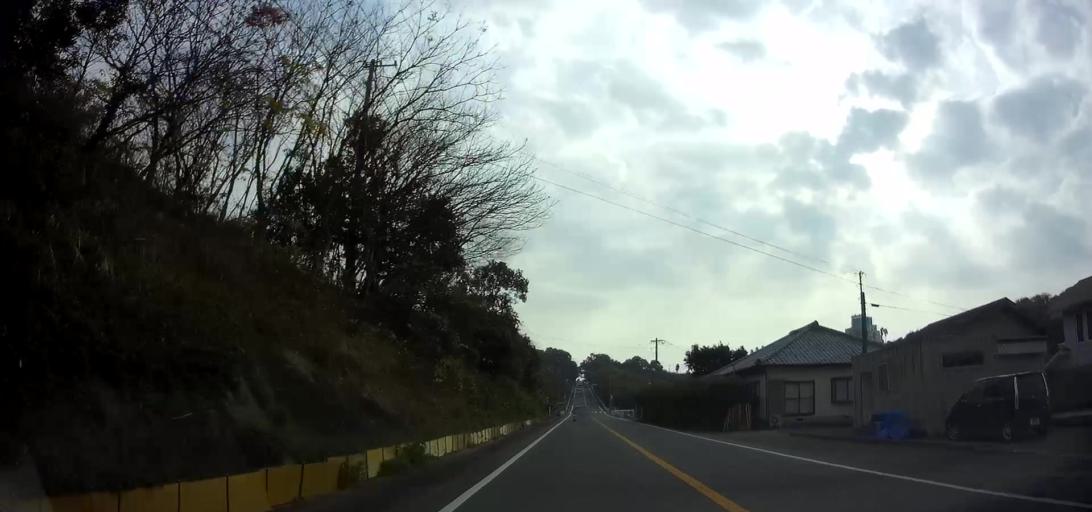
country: JP
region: Nagasaki
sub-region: Isahaya-shi
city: Isahaya
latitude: 32.7974
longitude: 130.0915
